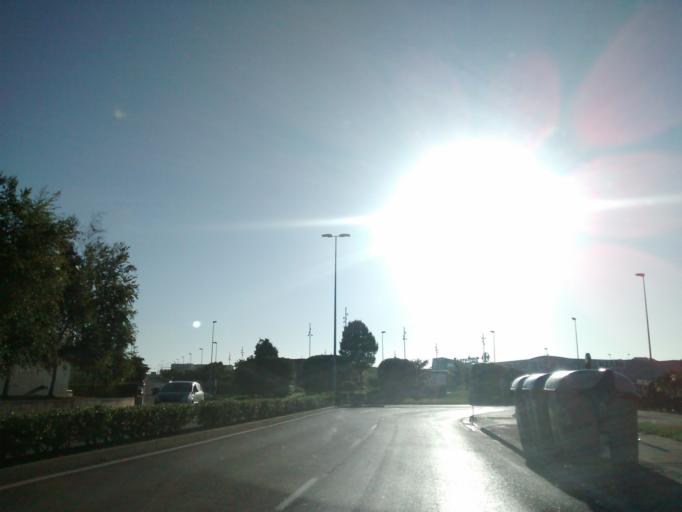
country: ES
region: Cantabria
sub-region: Provincia de Cantabria
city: Santa Cruz de Bezana
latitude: 43.4574
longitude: -3.8579
